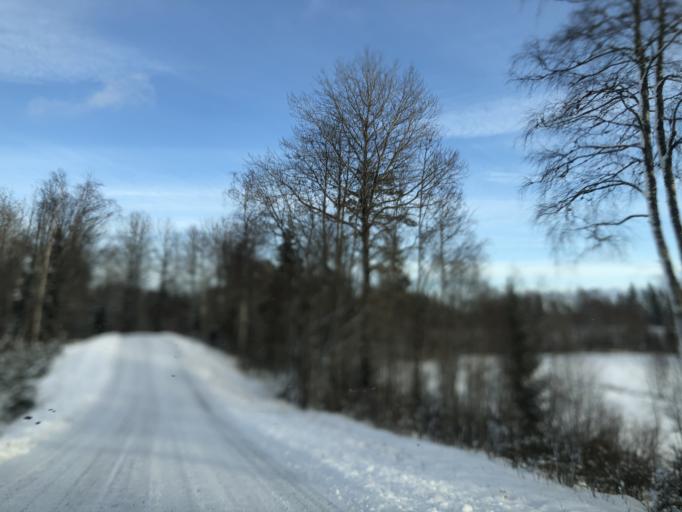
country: SE
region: Vaestra Goetaland
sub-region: Ulricehamns Kommun
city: Ulricehamn
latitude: 57.7702
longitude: 13.5223
